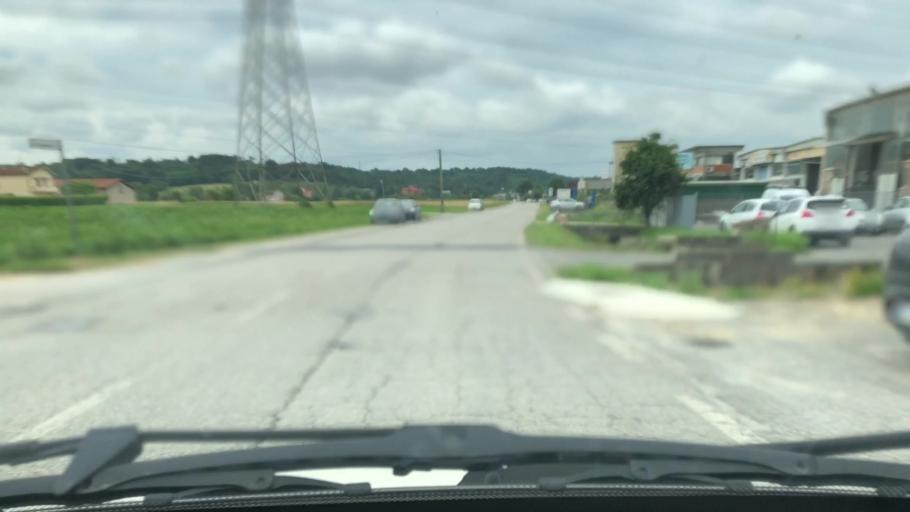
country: IT
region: Tuscany
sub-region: Province of Pisa
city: Bientina
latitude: 43.6995
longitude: 10.6240
